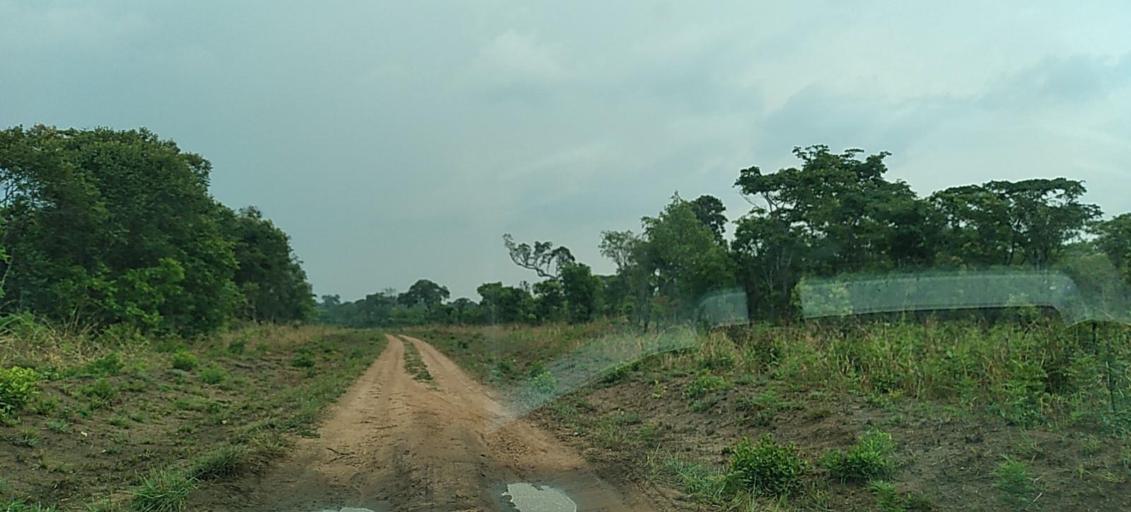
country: ZM
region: North-Western
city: Mwinilunga
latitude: -11.4425
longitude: 24.5925
